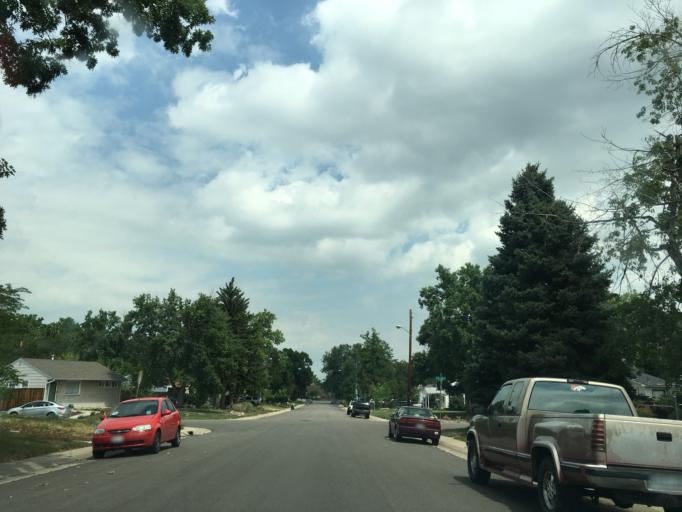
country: US
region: Colorado
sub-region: Arapahoe County
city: Sheridan
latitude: 39.6699
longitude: -105.0320
